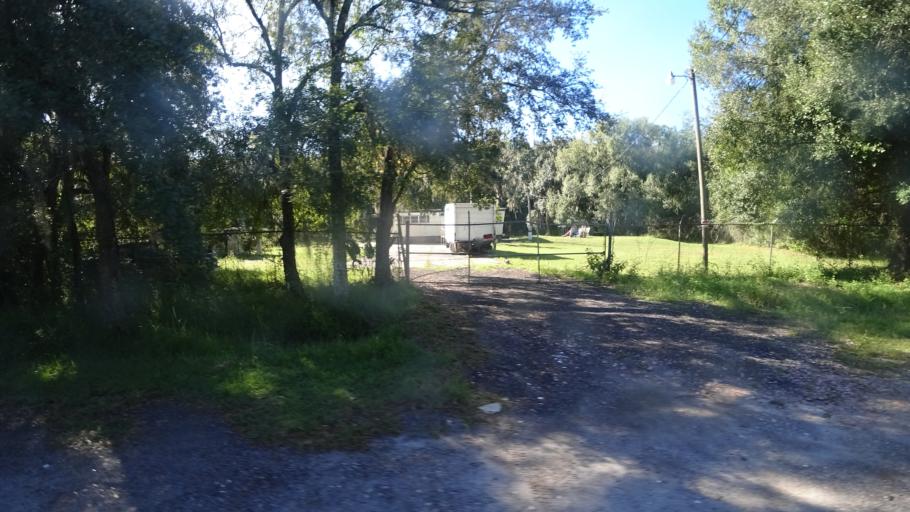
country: US
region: Florida
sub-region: Hillsborough County
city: Sun City Center
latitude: 27.6483
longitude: -82.3720
